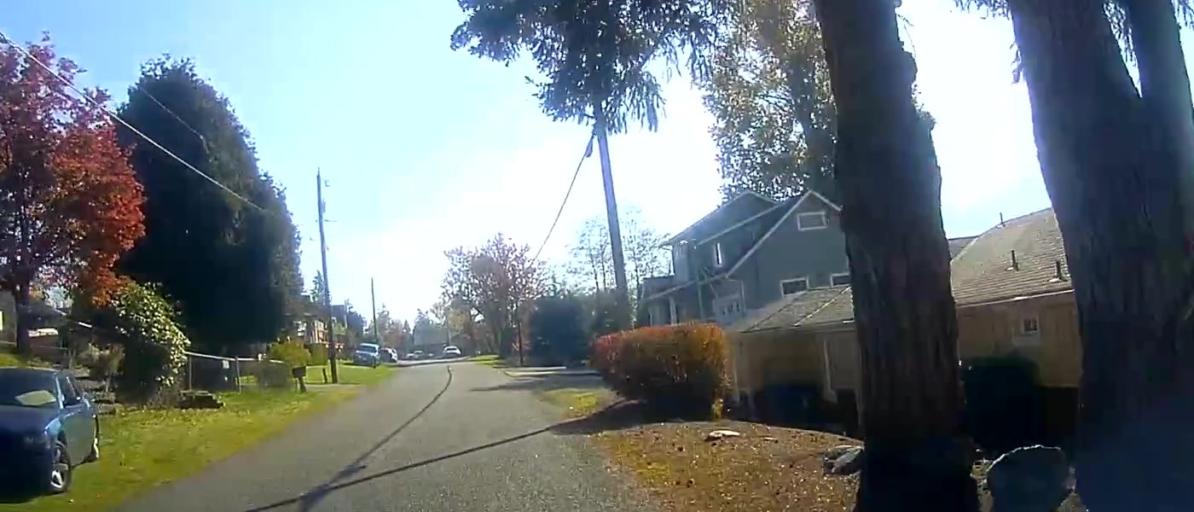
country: US
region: Washington
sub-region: Skagit County
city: Big Lake
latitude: 48.3971
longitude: -122.2395
